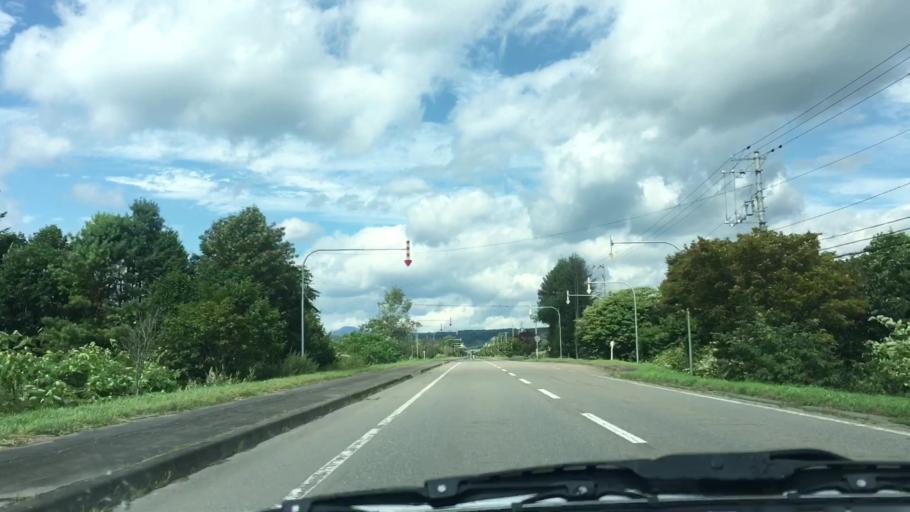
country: JP
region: Hokkaido
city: Otofuke
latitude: 43.2898
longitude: 143.3080
